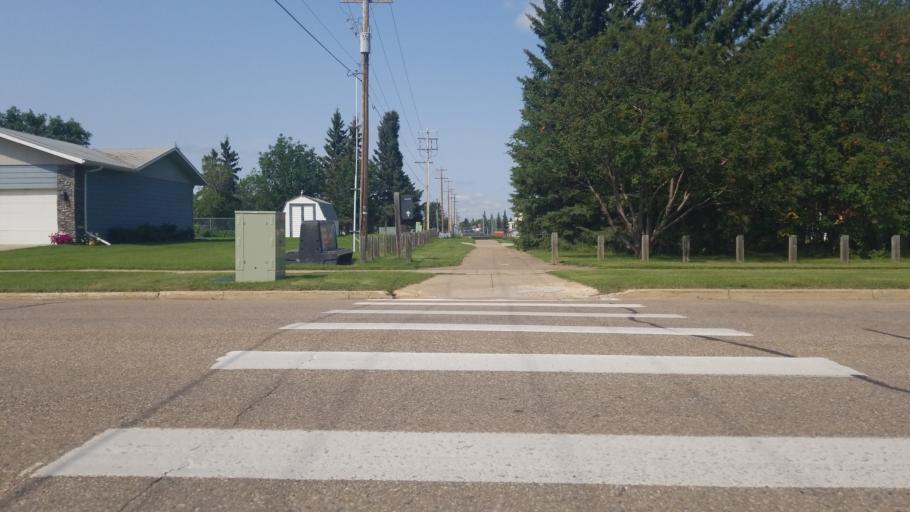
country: CA
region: Saskatchewan
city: Lloydminster
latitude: 53.2728
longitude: -110.0176
